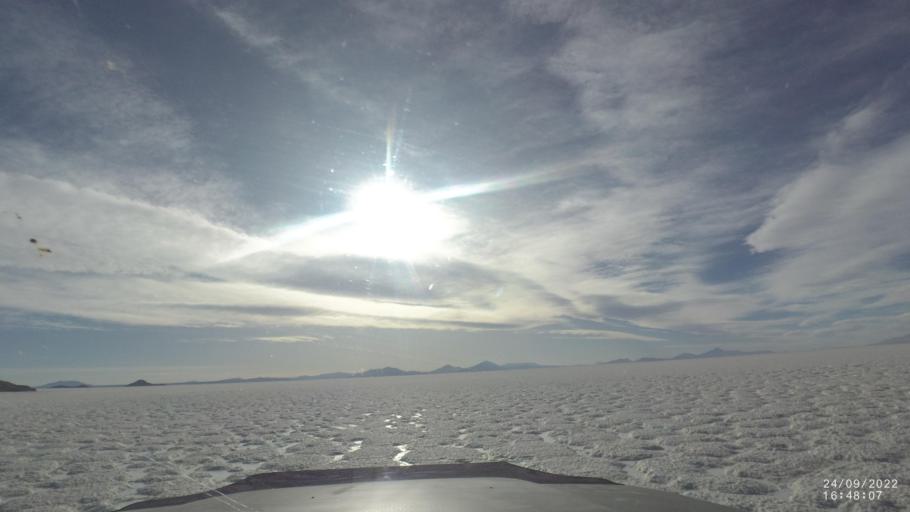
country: BO
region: Potosi
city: Colchani
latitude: -20.1318
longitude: -67.8087
